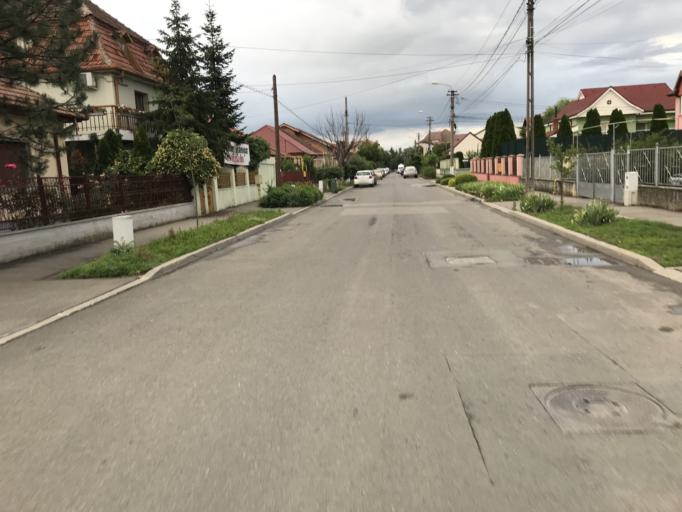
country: RO
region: Timis
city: Timisoara
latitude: 45.7731
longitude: 21.2347
